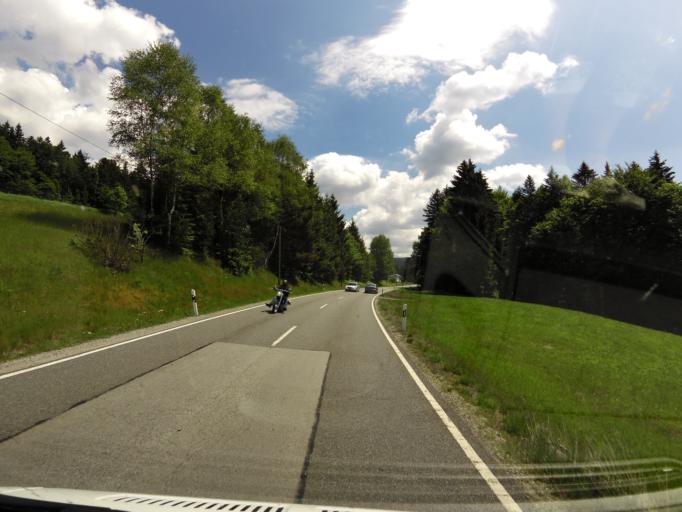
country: DE
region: Bavaria
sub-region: Lower Bavaria
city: Philippsreut
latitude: 48.8443
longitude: 13.6485
